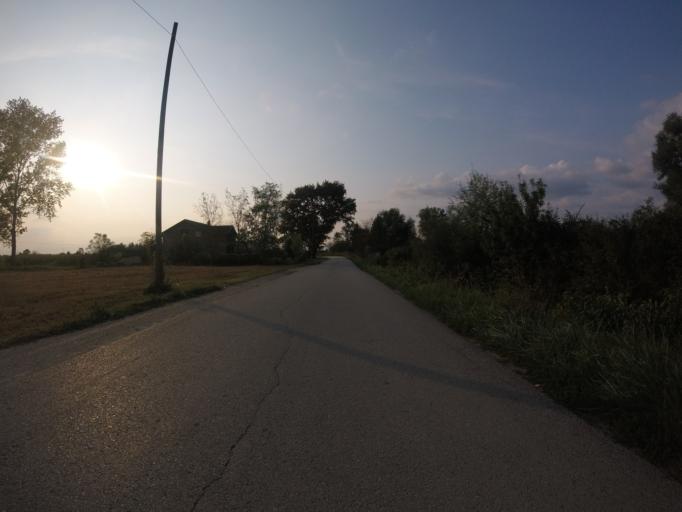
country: HR
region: Zagrebacka
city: Kuce
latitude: 45.7240
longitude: 16.2057
